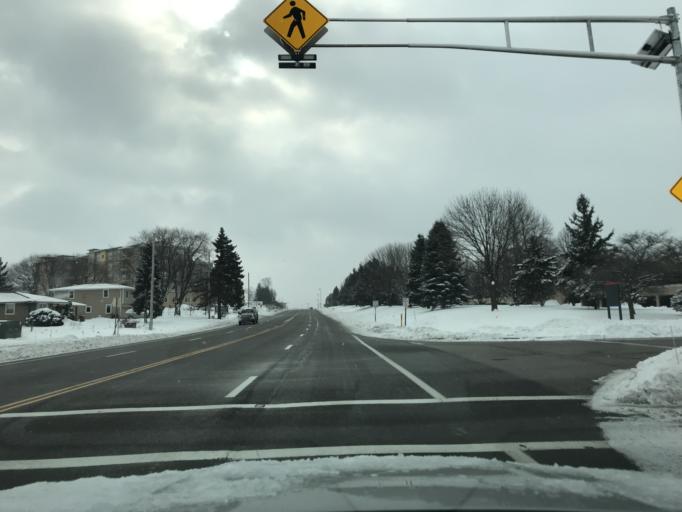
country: US
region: Wisconsin
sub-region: Dane County
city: Sun Prairie
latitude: 43.1583
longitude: -89.2852
